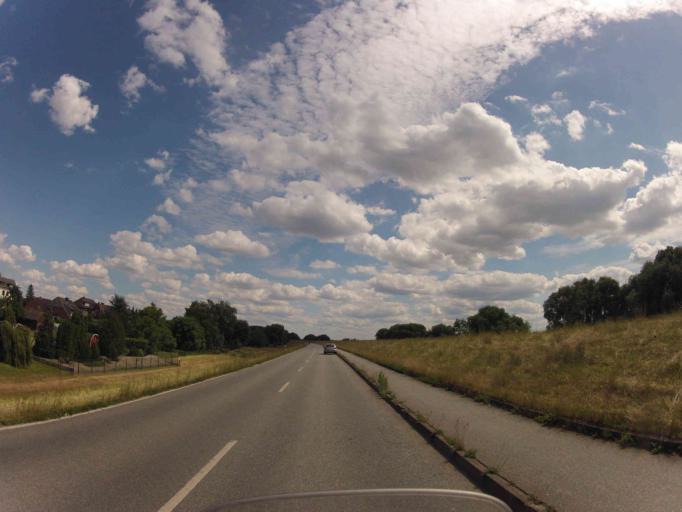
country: DE
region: Lower Saxony
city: Stelle
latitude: 53.4050
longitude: 10.1602
